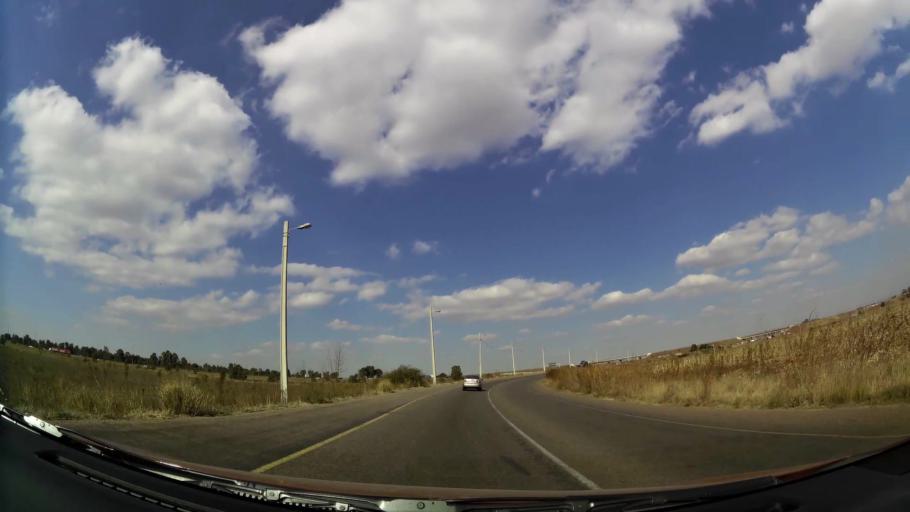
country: ZA
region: Gauteng
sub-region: Ekurhuleni Metropolitan Municipality
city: Tembisa
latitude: -25.9842
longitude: 28.2482
